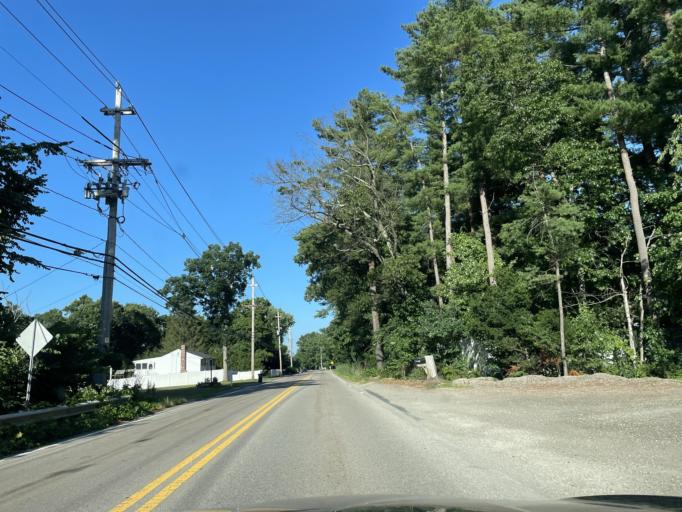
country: US
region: Massachusetts
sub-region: Norfolk County
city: Wrentham
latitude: 42.0730
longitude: -71.3444
